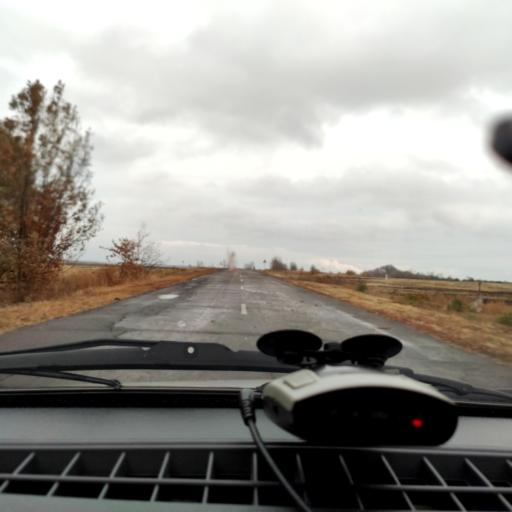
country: RU
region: Voronezj
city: Kolodeznyy
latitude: 51.2422
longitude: 38.9890
